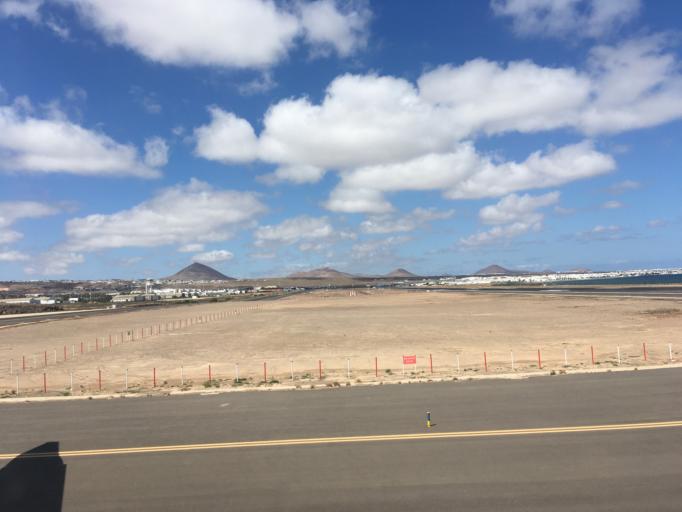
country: ES
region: Canary Islands
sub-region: Provincia de Las Palmas
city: Tias
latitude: 28.9363
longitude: -13.6117
